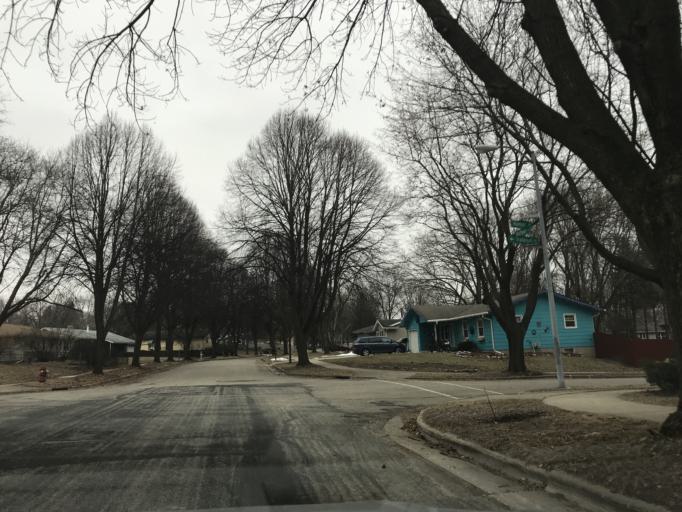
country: US
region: Wisconsin
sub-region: Dane County
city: Monona
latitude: 43.1011
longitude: -89.2975
